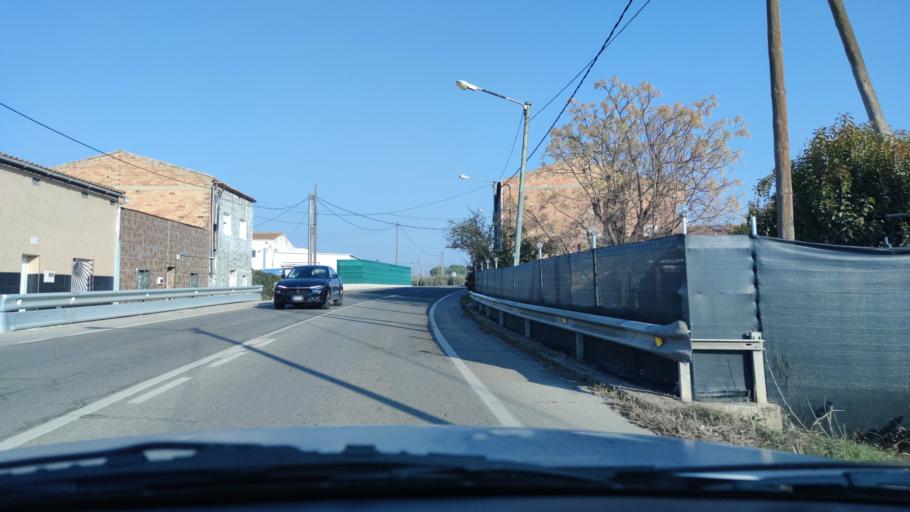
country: ES
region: Catalonia
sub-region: Provincia de Lleida
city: Lleida
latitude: 41.6430
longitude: 0.6353
